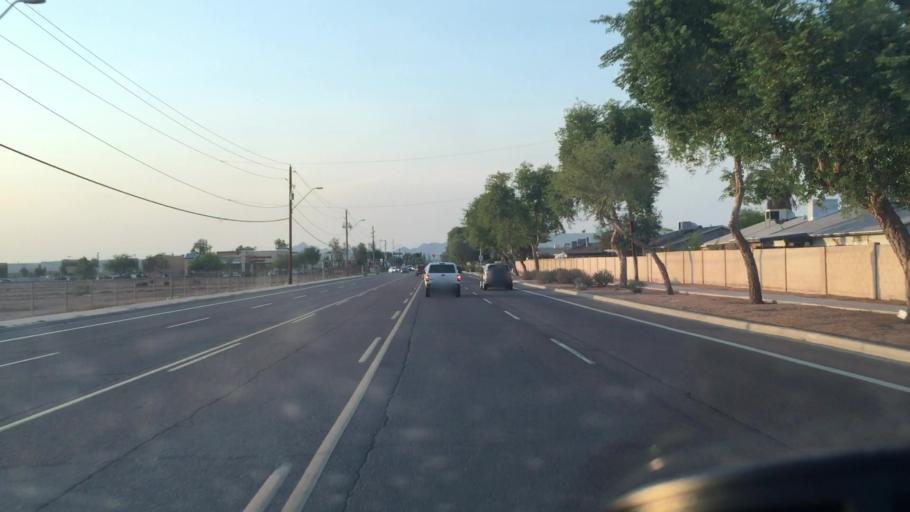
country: US
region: Arizona
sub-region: Maricopa County
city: Guadalupe
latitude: 33.3892
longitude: -111.9955
